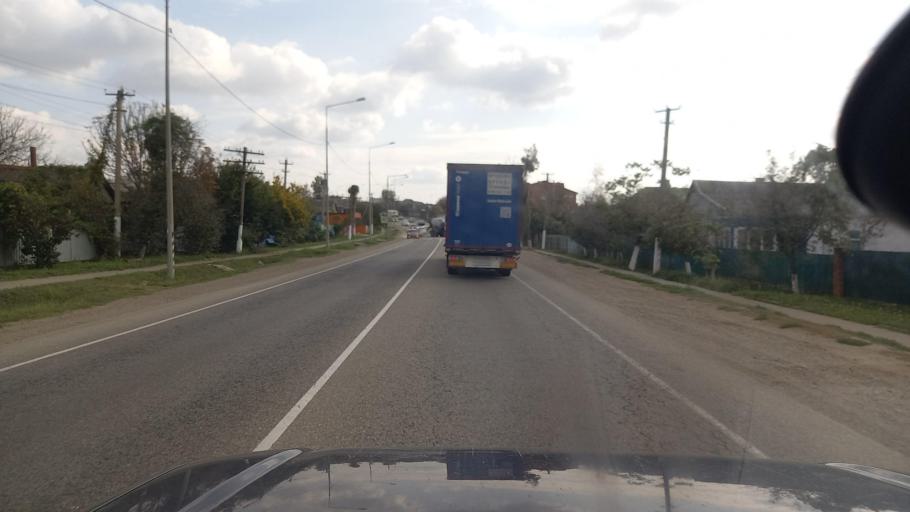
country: RU
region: Krasnodarskiy
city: Kholmskiy
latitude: 44.8494
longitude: 38.4032
